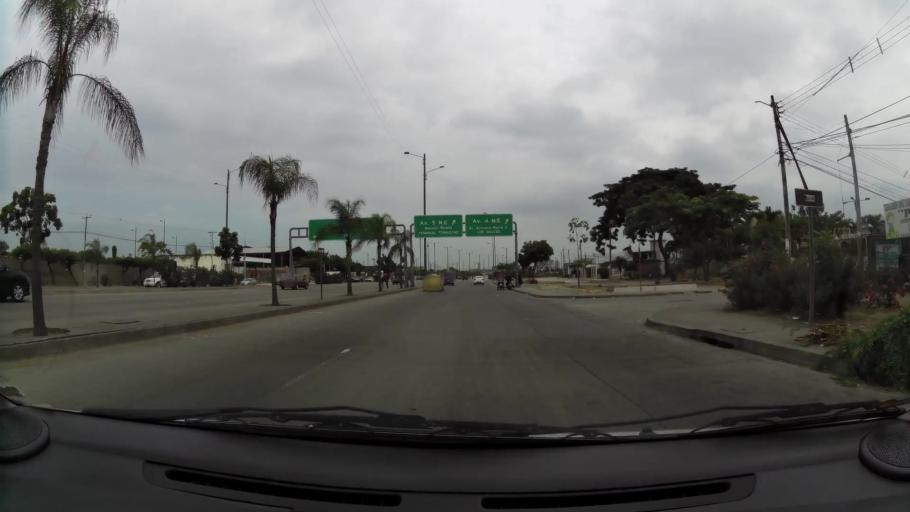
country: EC
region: Guayas
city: Eloy Alfaro
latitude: -2.1361
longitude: -79.8820
